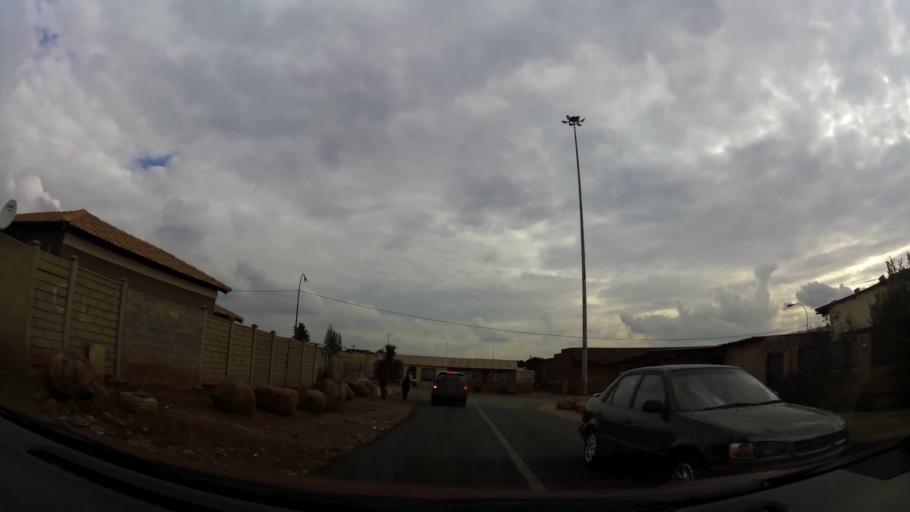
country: ZA
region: Gauteng
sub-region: City of Johannesburg Metropolitan Municipality
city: Soweto
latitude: -26.2440
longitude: 27.8508
